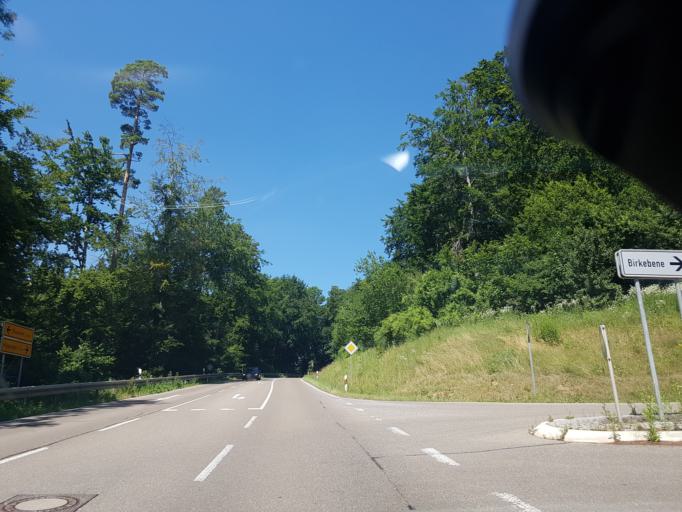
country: DE
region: Baden-Wuerttemberg
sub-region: Tuebingen Region
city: Dornstadt
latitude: 48.4227
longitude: 9.8791
